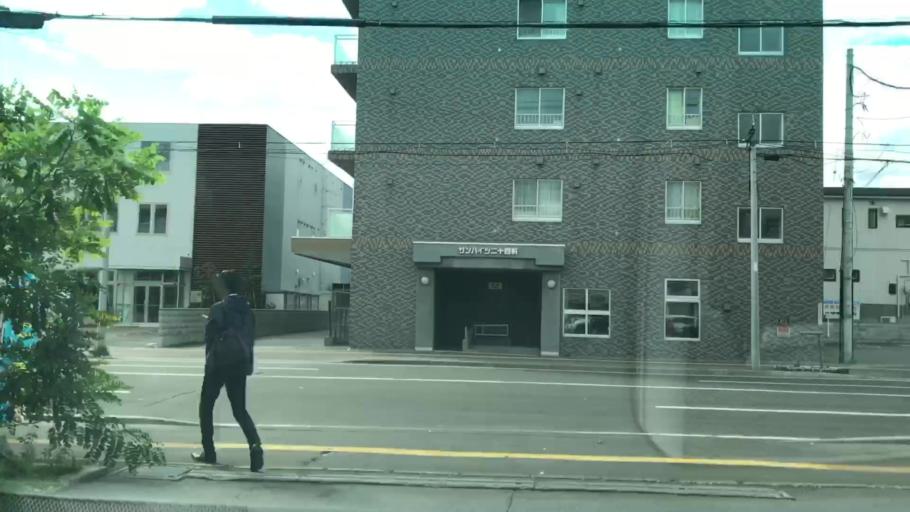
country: JP
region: Hokkaido
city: Sapporo
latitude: 43.0777
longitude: 141.3106
